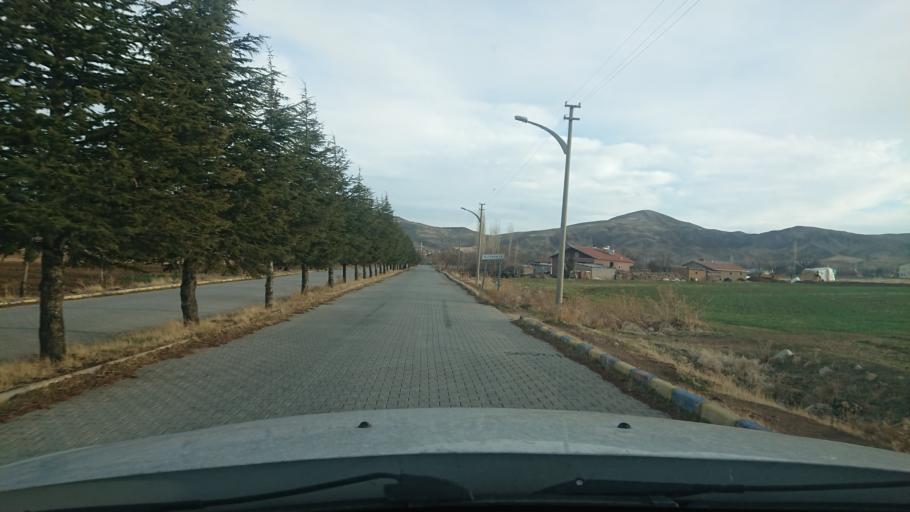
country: TR
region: Aksaray
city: Acipinar
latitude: 38.6078
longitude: 33.7757
